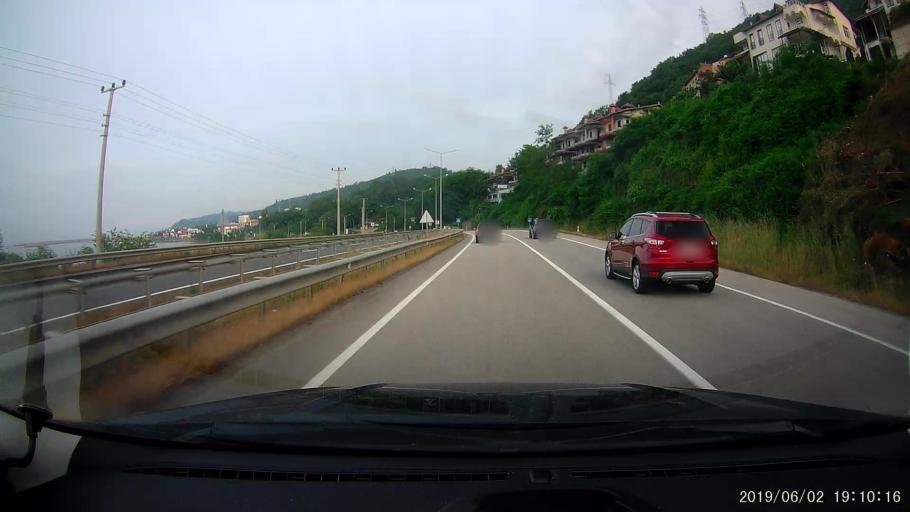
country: TR
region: Ordu
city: Gulyali
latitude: 40.9703
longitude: 38.0419
